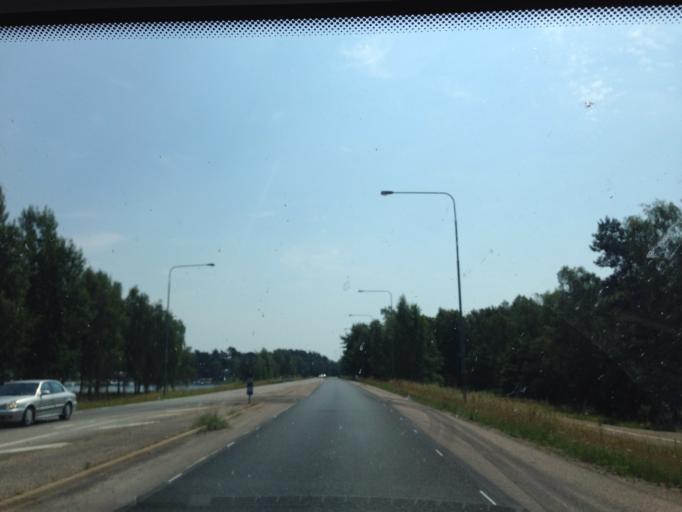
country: SE
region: Kalmar
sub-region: Kalmar Kommun
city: Kalmar
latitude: 56.6782
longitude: 16.3610
